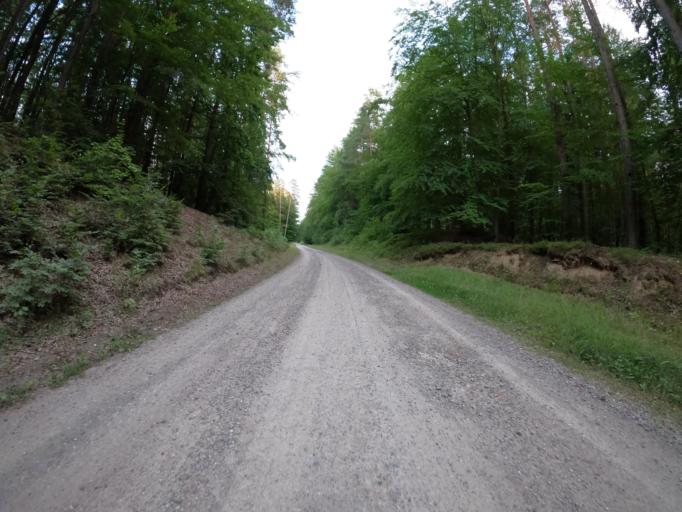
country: PL
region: West Pomeranian Voivodeship
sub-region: Powiat koszalinski
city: Sianow
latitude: 54.1032
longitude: 16.3716
